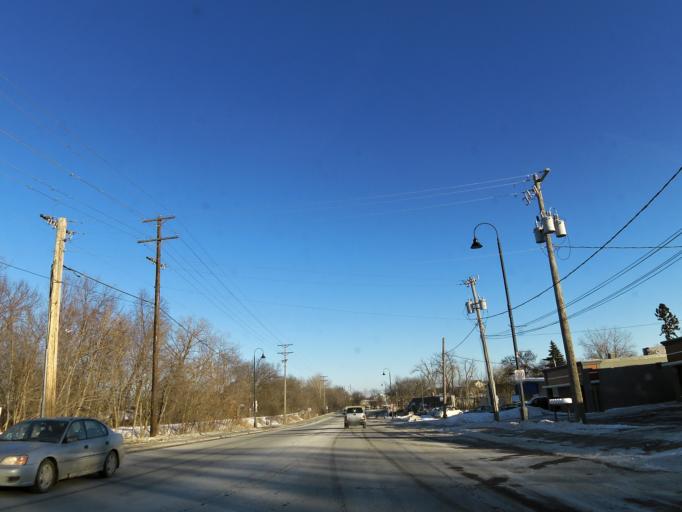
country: US
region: Minnesota
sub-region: Hennepin County
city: Spring Park
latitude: 44.9370
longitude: -93.6476
